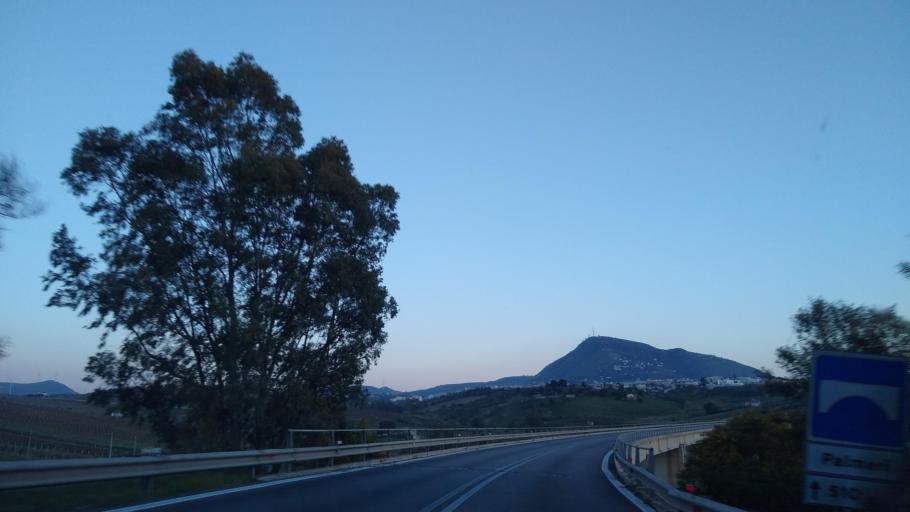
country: IT
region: Sicily
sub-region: Trapani
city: Alcamo
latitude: 38.0096
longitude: 12.9619
